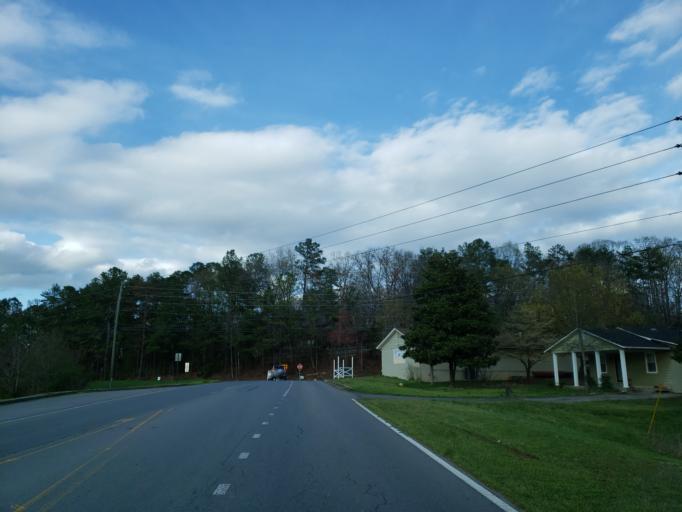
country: US
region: Georgia
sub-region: Bartow County
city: Cartersville
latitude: 34.2403
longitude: -84.8100
